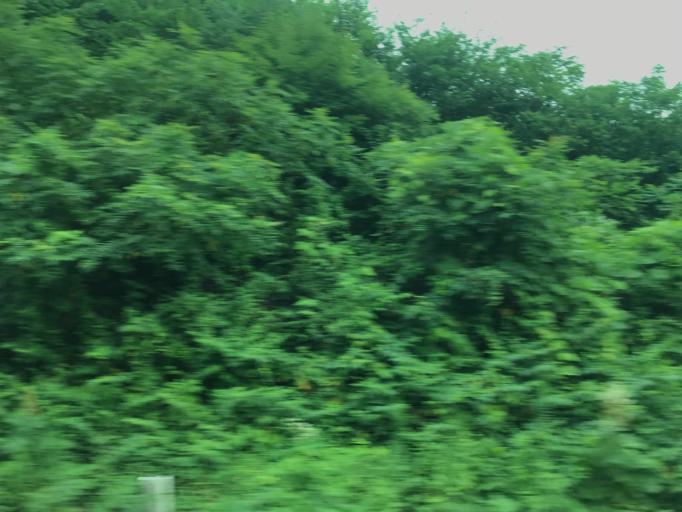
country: JP
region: Tochigi
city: Kuroiso
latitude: 37.0281
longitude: 140.1320
